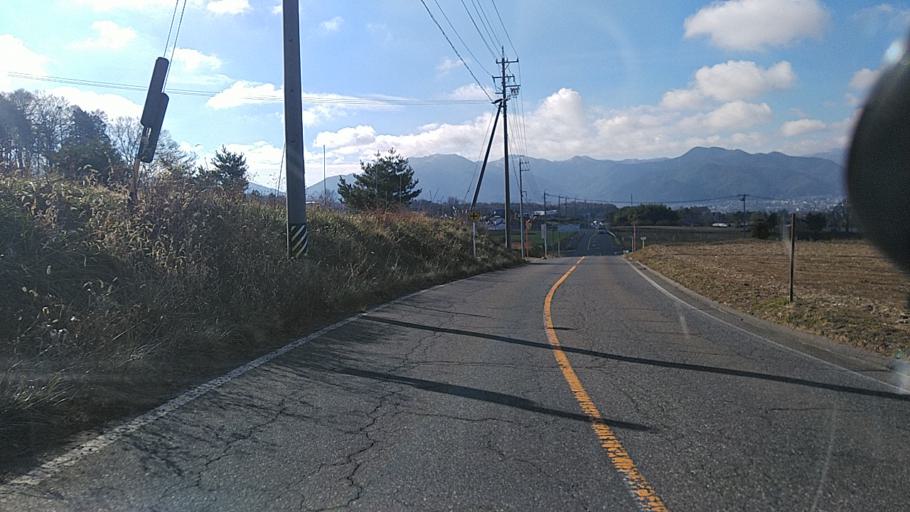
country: JP
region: Nagano
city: Shiojiri
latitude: 36.1328
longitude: 137.9877
